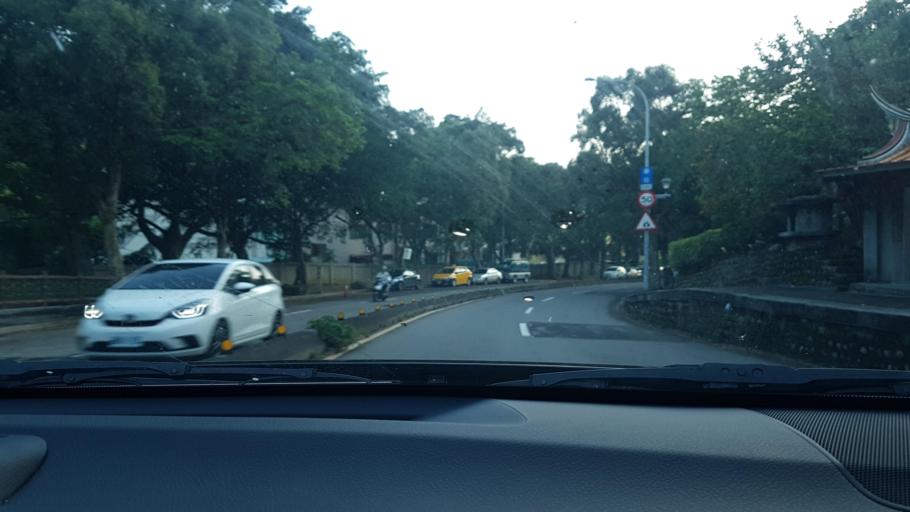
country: TW
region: Taipei
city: Taipei
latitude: 25.1050
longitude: 121.5571
